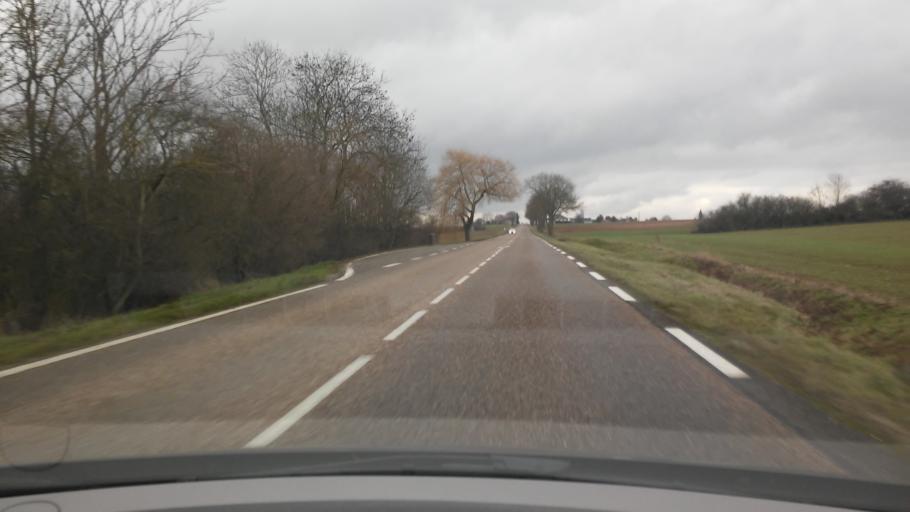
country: FR
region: Lorraine
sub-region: Departement de la Moselle
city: Retonfey
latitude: 49.1151
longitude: 6.2906
